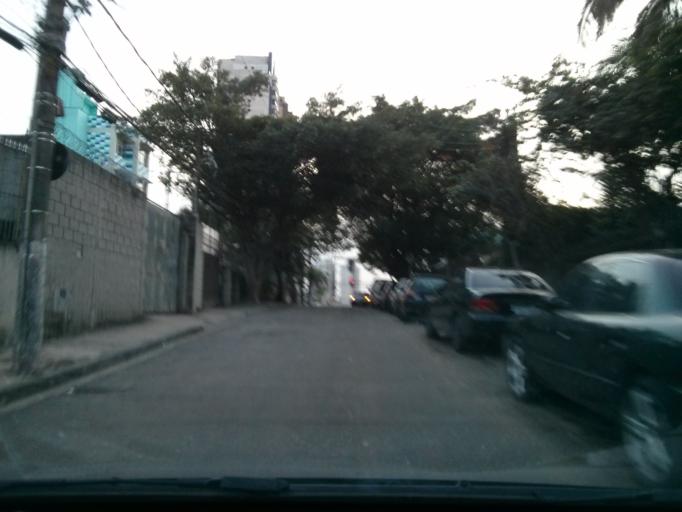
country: BR
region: Sao Paulo
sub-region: Taboao Da Serra
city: Taboao da Serra
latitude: -23.6079
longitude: -46.7247
